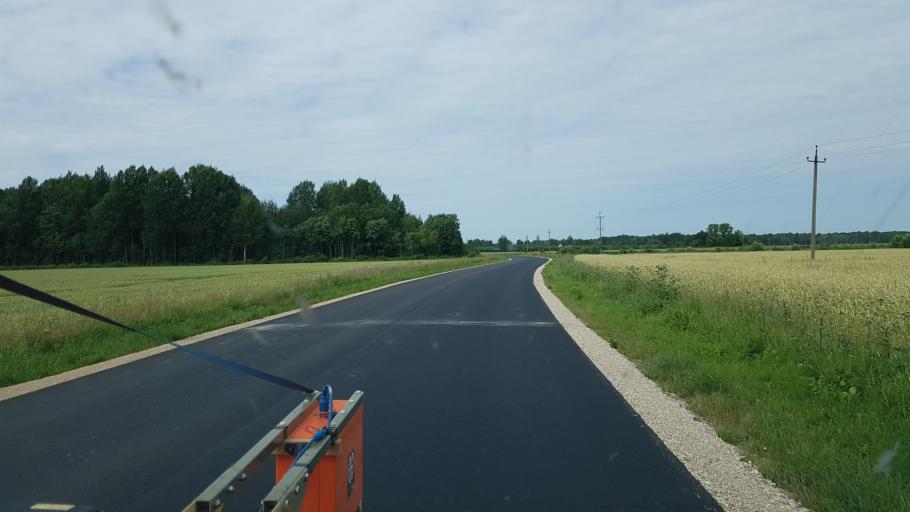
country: EE
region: Paernumaa
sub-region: Halinga vald
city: Parnu-Jaagupi
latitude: 58.6239
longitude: 24.3710
